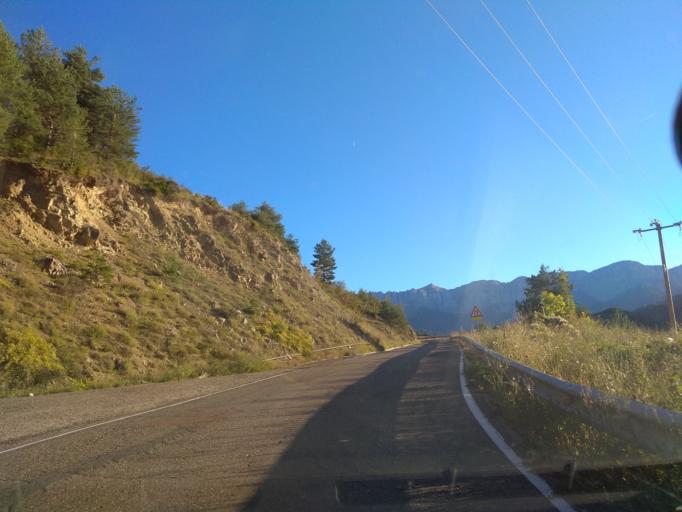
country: ES
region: Catalonia
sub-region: Provincia de Lleida
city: Lles de Cerdanya
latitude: 42.3543
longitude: 1.6897
